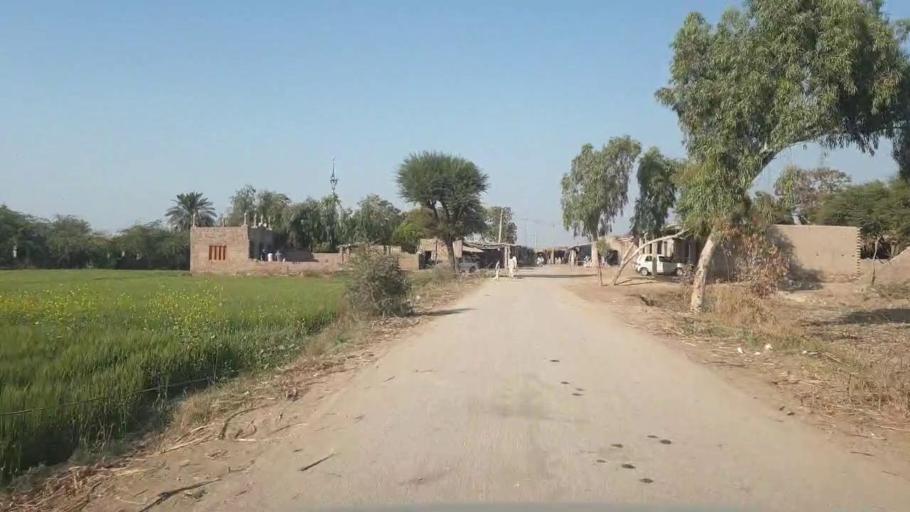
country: PK
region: Sindh
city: Chambar
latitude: 25.2929
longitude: 68.8637
